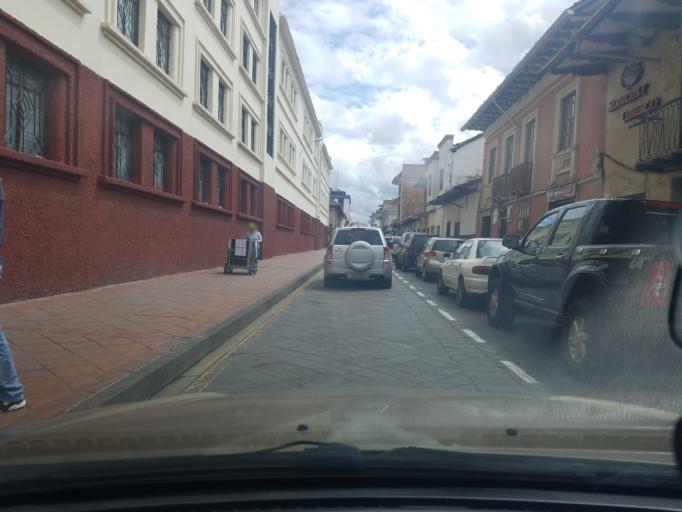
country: EC
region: Azuay
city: Cuenca
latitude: -2.8993
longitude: -79.0023
